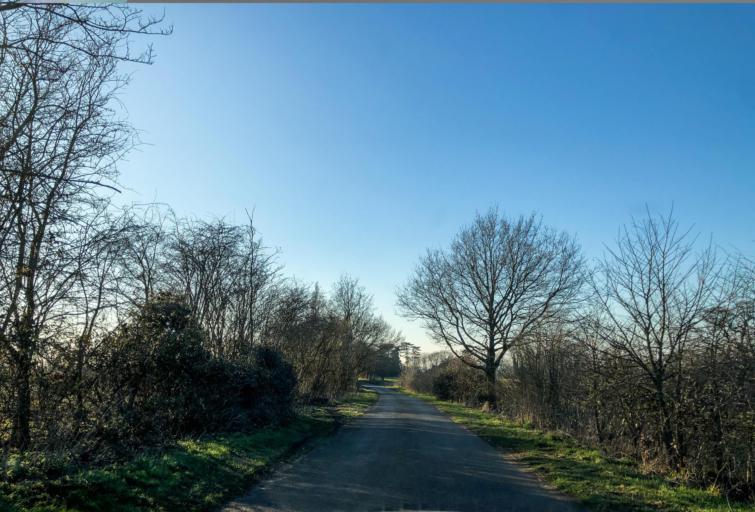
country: GB
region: England
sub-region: Warwickshire
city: Warwick
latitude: 52.2476
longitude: -1.5907
